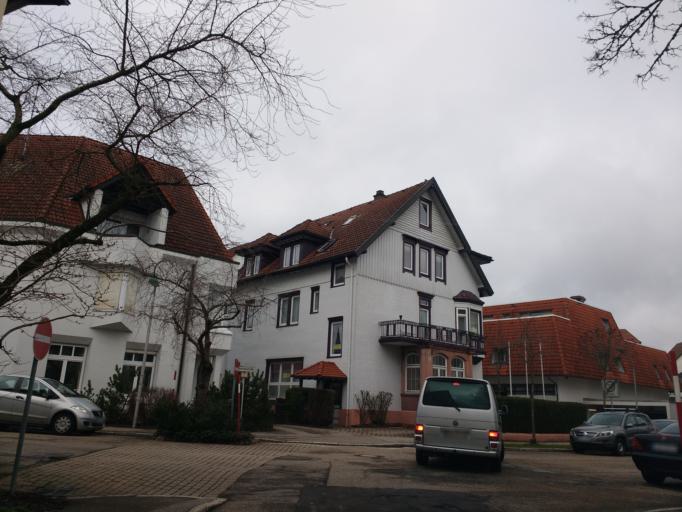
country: DE
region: Baden-Wuerttemberg
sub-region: Karlsruhe Region
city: Freudenstadt
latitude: 48.4661
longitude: 8.4125
